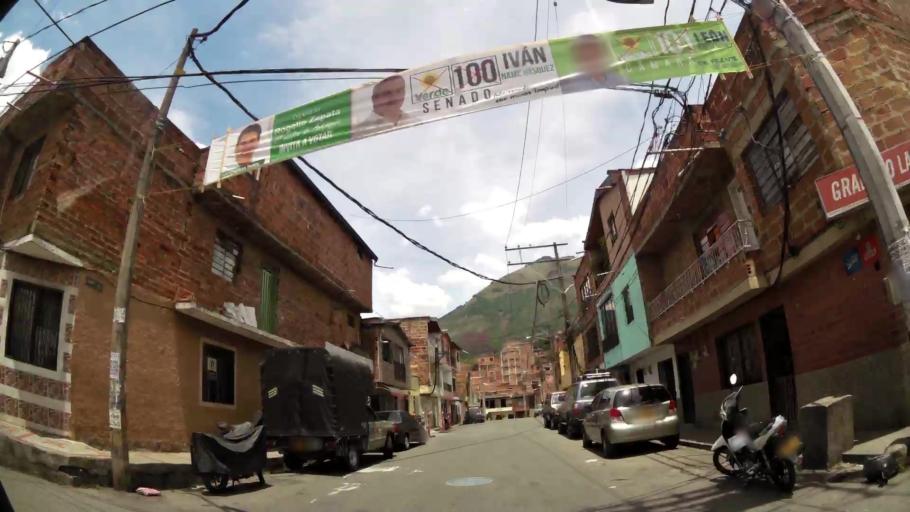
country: CO
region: Antioquia
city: Bello
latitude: 6.3414
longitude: -75.5569
